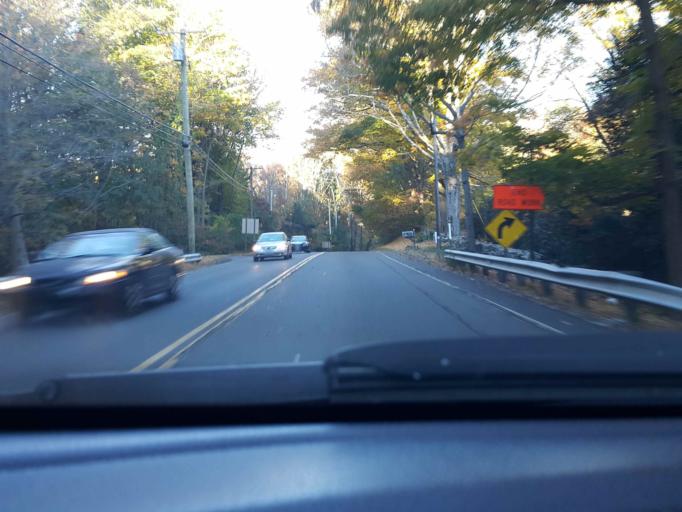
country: US
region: Connecticut
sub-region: New Haven County
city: Woodbridge
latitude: 41.3786
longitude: -73.0070
